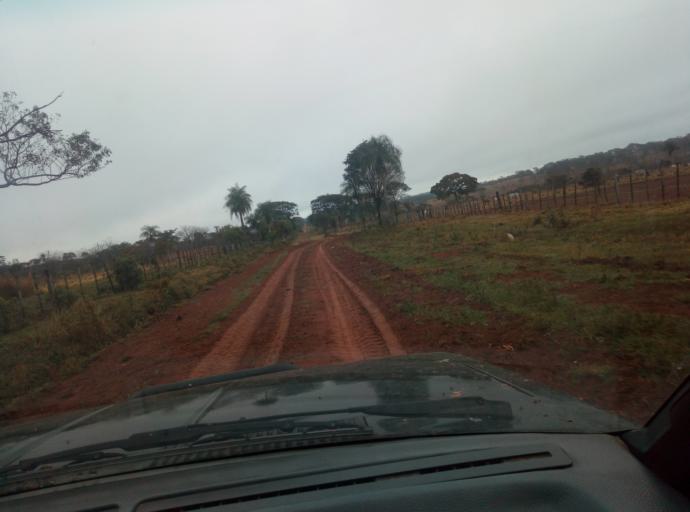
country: PY
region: Caaguazu
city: Carayao
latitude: -25.1937
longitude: -56.3274
